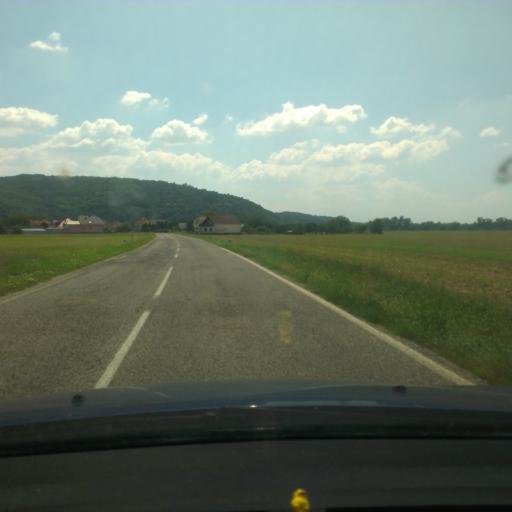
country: SK
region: Trnavsky
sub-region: Okres Trnava
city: Piestany
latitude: 48.5133
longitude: 17.8245
